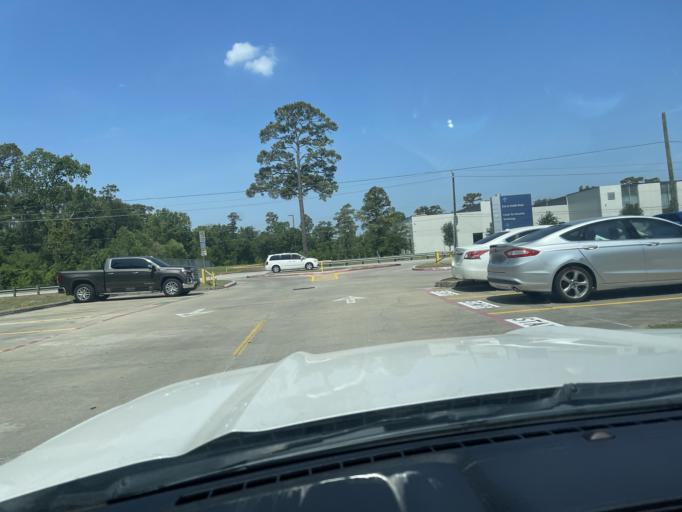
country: US
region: Texas
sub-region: Harris County
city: Cloverleaf
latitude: 29.8091
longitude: -95.1819
